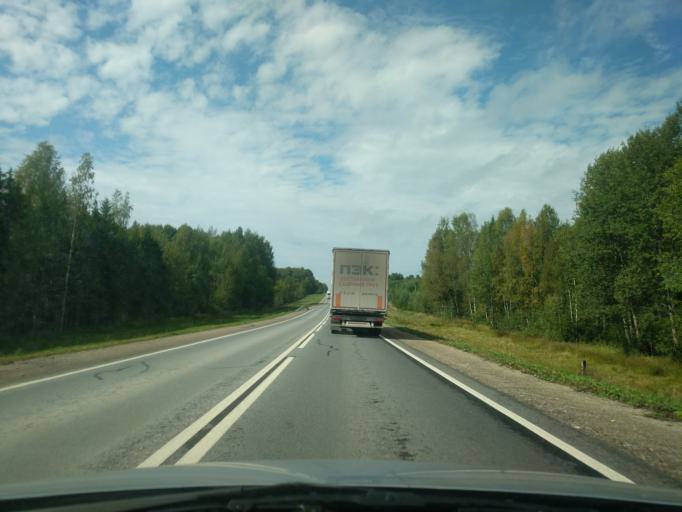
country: RU
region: Kostroma
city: Sudislavl'
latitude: 57.8612
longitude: 41.7718
